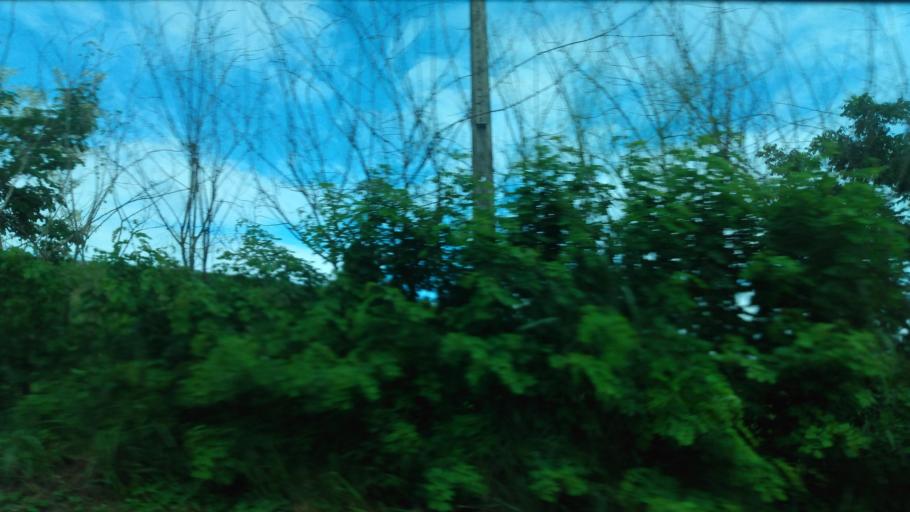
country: BR
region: Pernambuco
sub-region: Catende
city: Catende
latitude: -8.7034
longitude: -35.7463
